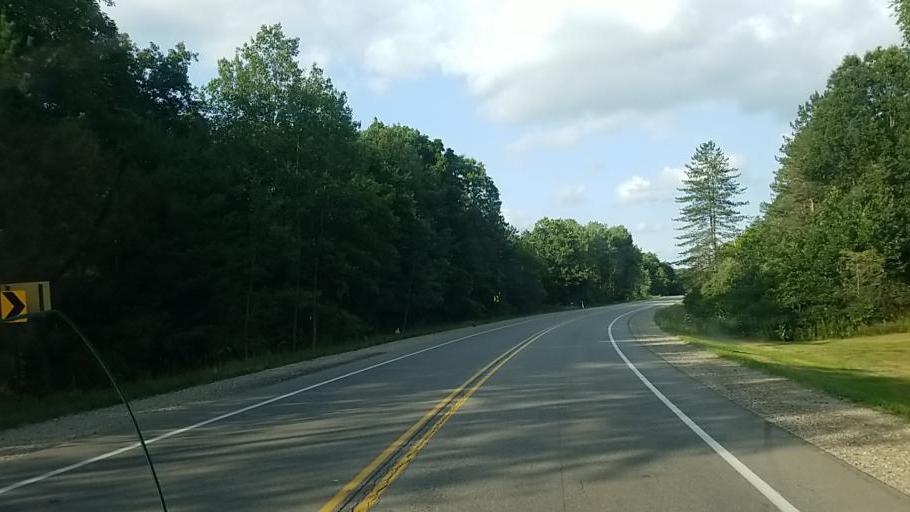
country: US
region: Michigan
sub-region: Kent County
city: Lowell
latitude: 42.9026
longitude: -85.3698
